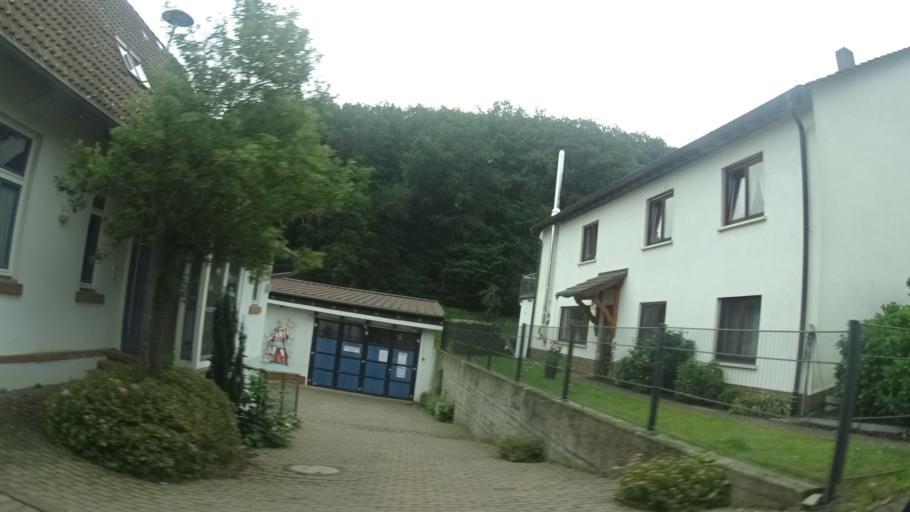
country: DE
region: Bavaria
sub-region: Regierungsbezirk Unterfranken
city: Johannesberg
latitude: 50.0714
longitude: 9.1155
